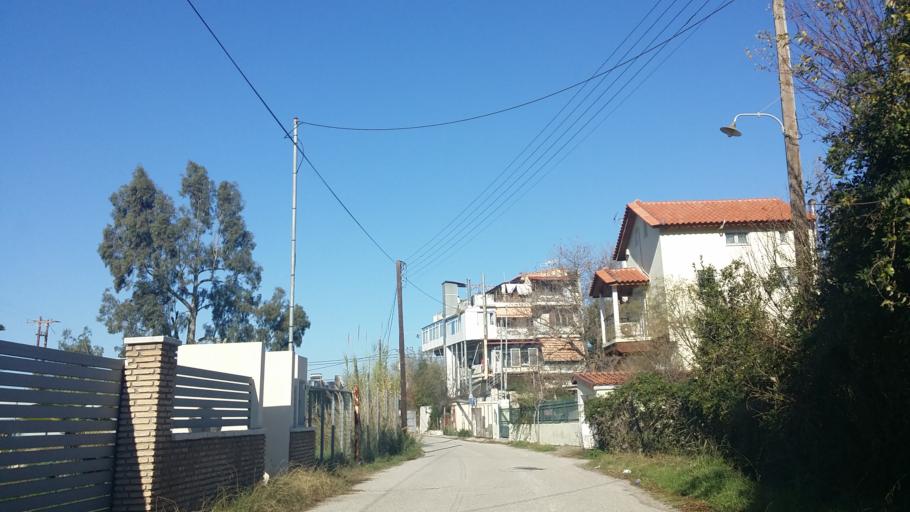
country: GR
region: West Greece
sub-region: Nomos Achaias
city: Temeni
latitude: 38.1995
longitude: 22.1799
